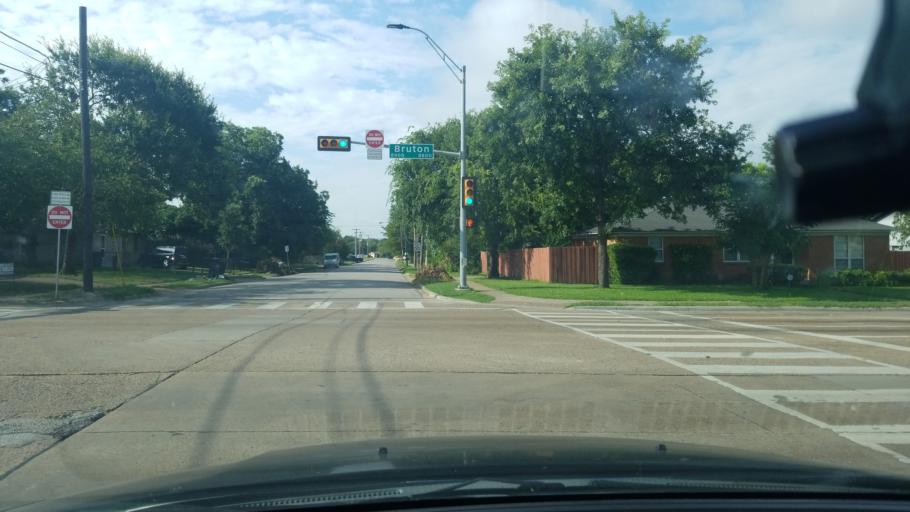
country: US
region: Texas
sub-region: Dallas County
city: Balch Springs
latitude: 32.7488
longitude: -96.6699
